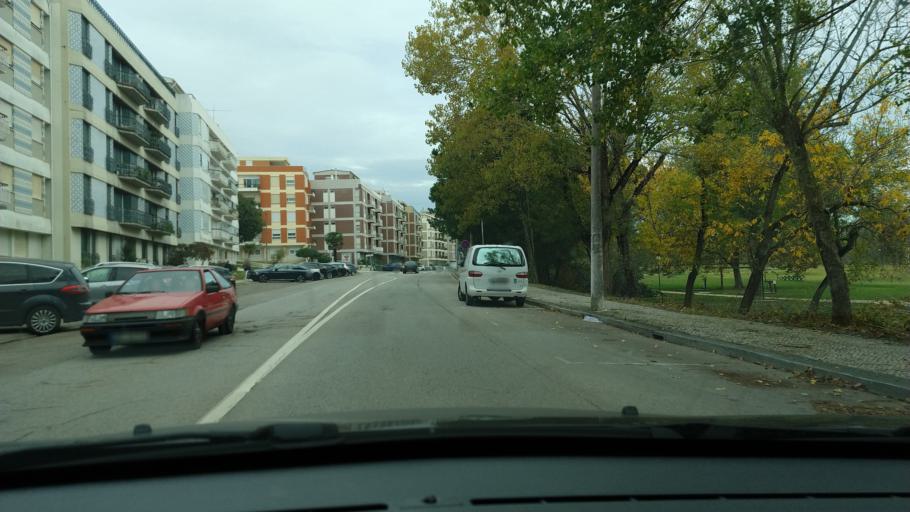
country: PT
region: Coimbra
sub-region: Figueira da Foz
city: Figueira da Foz
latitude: 40.1520
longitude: -8.8621
